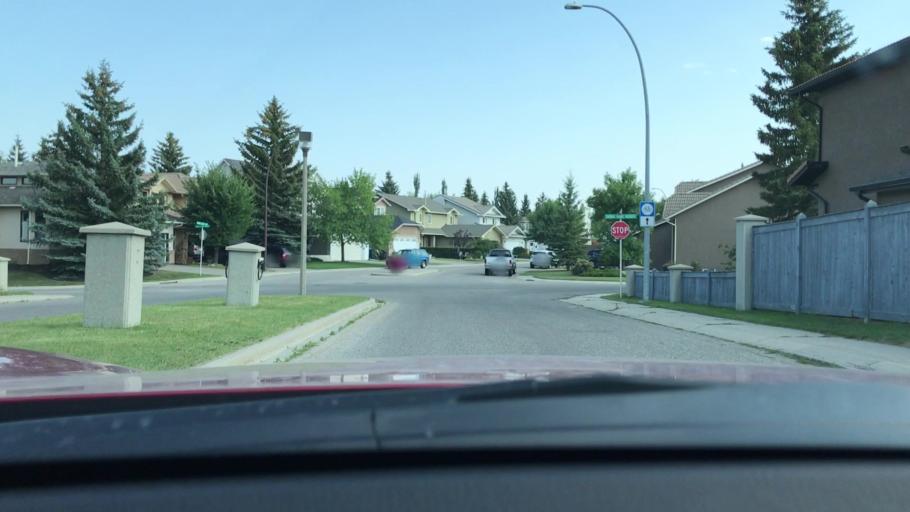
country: CA
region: Alberta
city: Calgary
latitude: 51.0303
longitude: -114.1745
